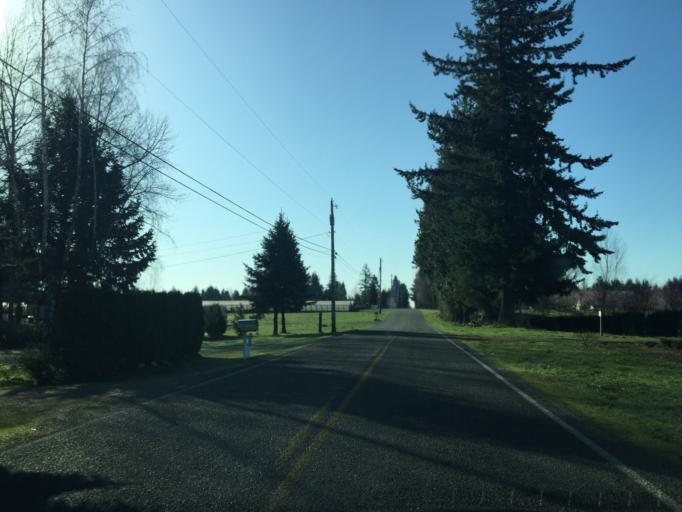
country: US
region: Washington
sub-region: Whatcom County
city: Lynden
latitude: 48.8954
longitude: -122.4969
